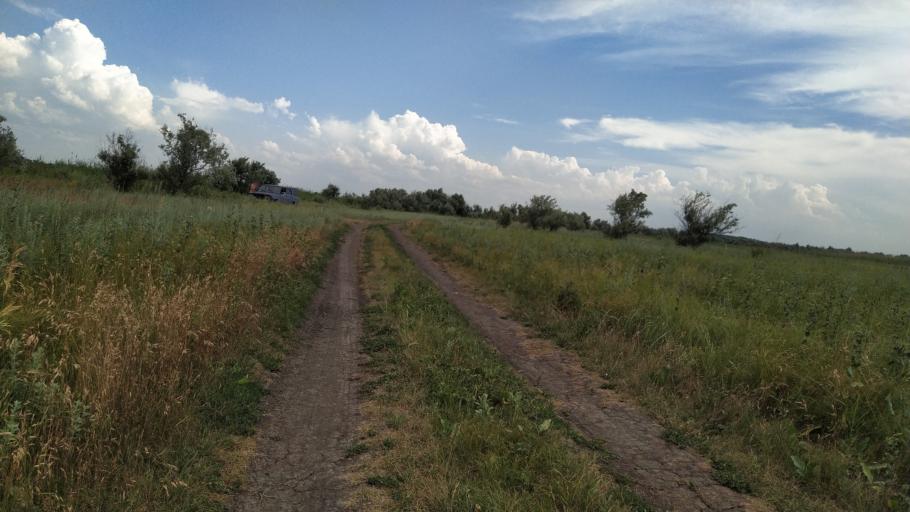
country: RU
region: Rostov
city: Kuleshovka
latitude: 47.1293
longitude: 39.6294
